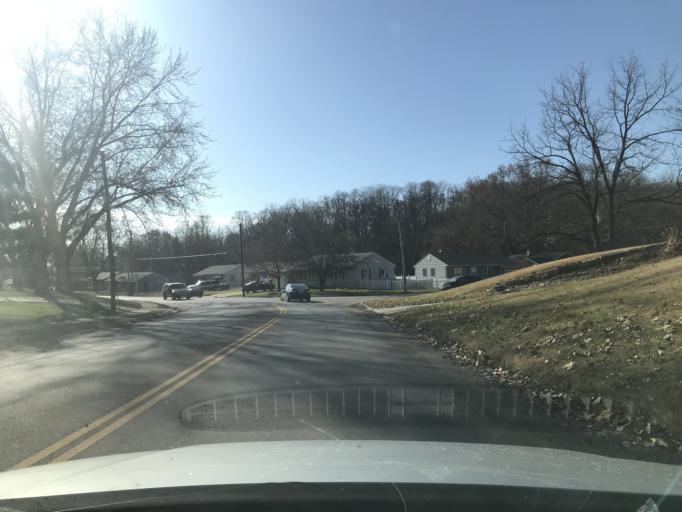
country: US
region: Iowa
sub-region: Scott County
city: Davenport
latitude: 41.5267
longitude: -90.6159
